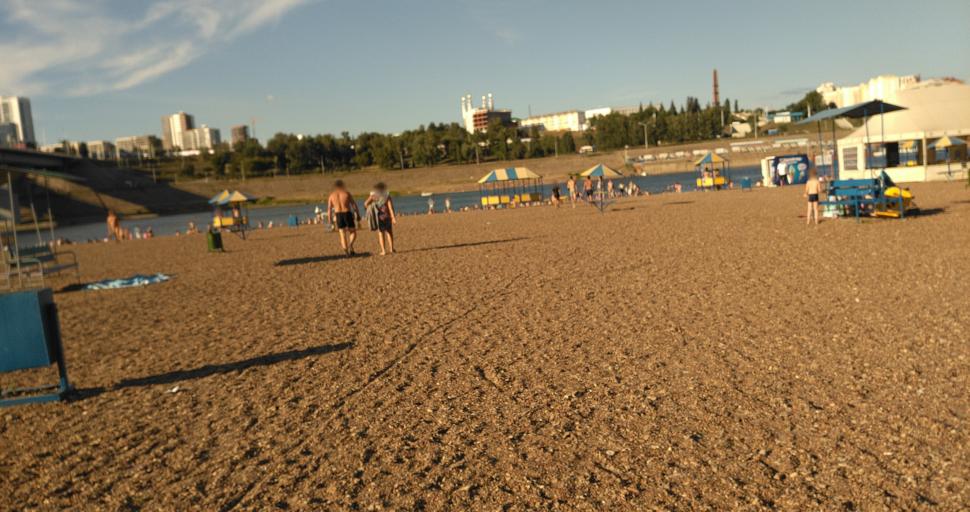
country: RU
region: Bashkortostan
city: Ufa
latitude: 54.7078
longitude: 55.9555
